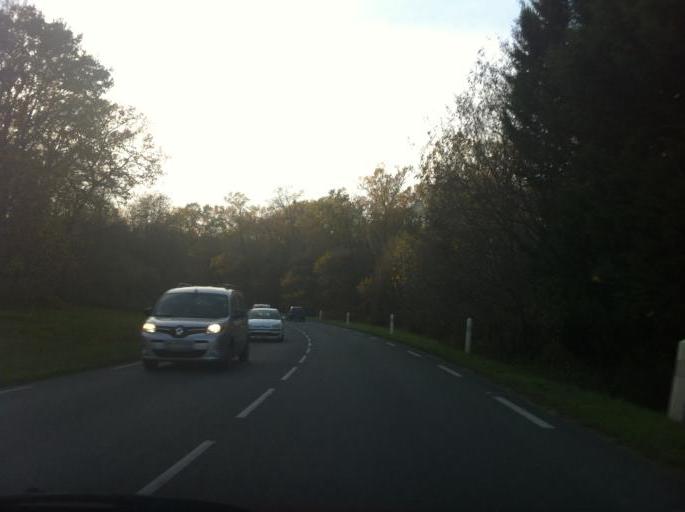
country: FR
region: Aquitaine
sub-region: Departement de la Dordogne
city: Tocane-Saint-Apre
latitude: 45.2509
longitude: 0.5180
